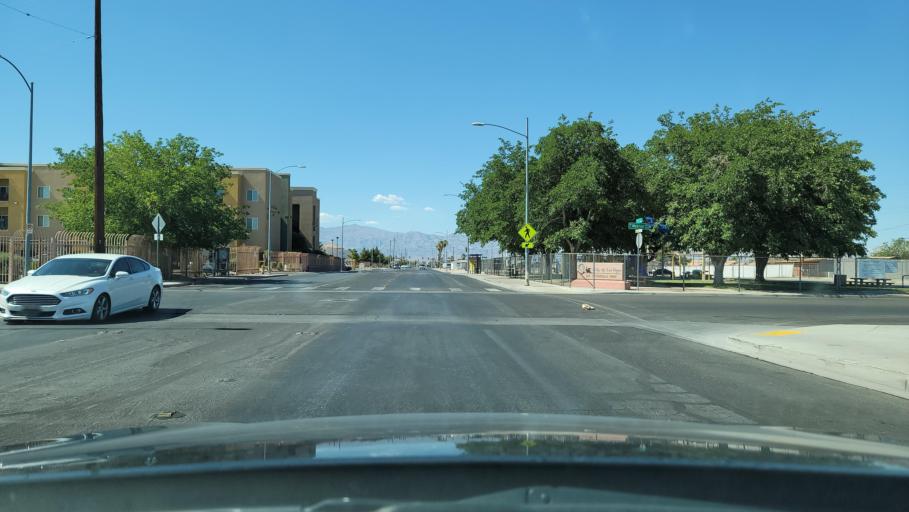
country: US
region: Nevada
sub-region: Clark County
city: Las Vegas
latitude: 36.1846
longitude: -115.1519
